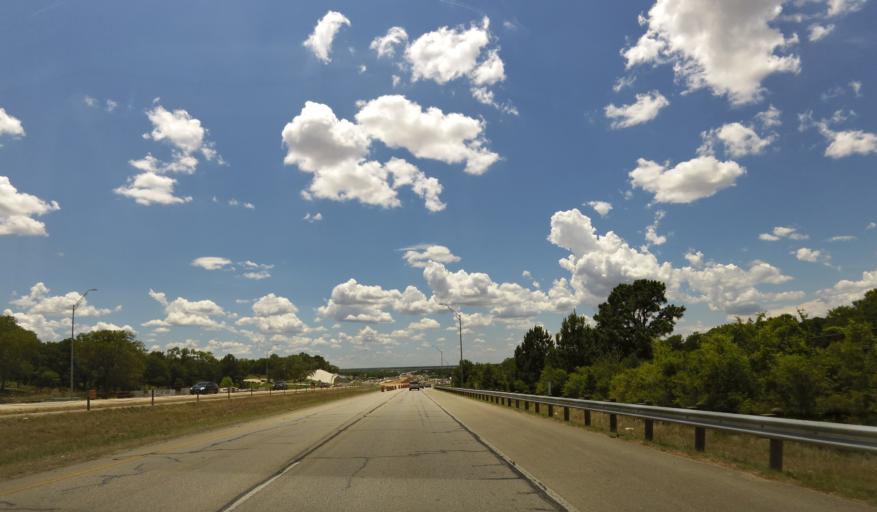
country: US
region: Texas
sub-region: Bastrop County
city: Bastrop
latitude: 30.1052
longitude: -97.3011
